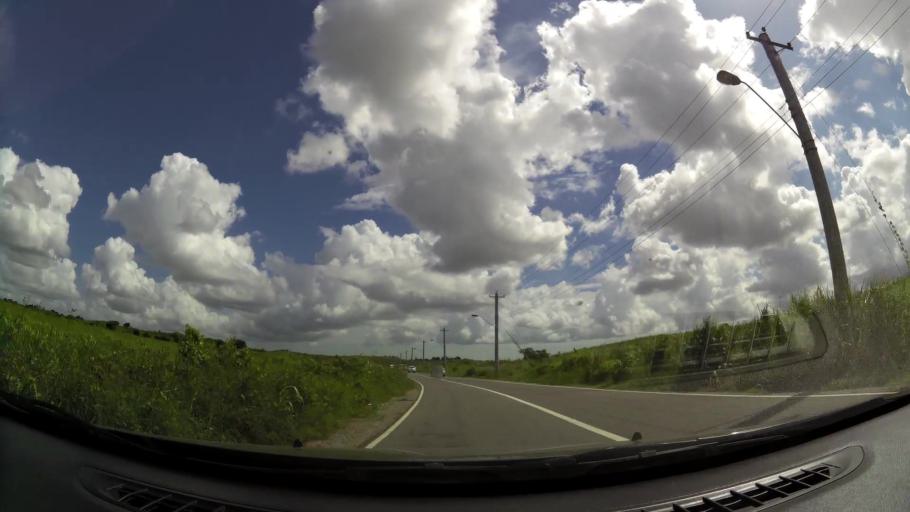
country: TT
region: Penal/Debe
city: Debe
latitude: 10.2353
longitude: -61.4959
